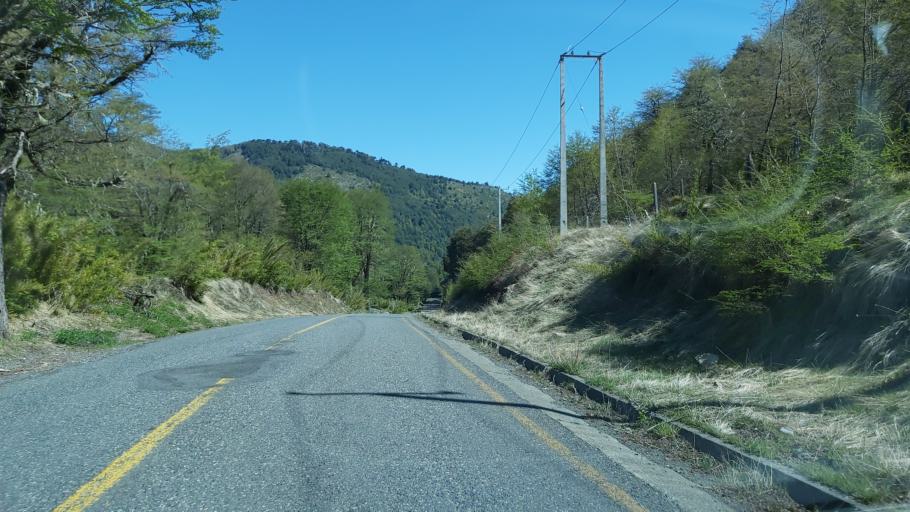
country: CL
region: Araucania
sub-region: Provincia de Cautin
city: Vilcun
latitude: -38.4564
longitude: -71.5159
